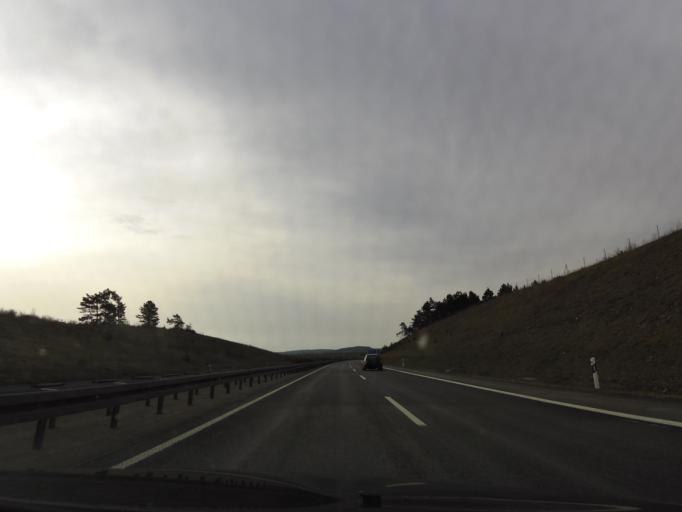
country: DE
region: Thuringia
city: Eisfeld
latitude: 50.4398
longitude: 10.8807
